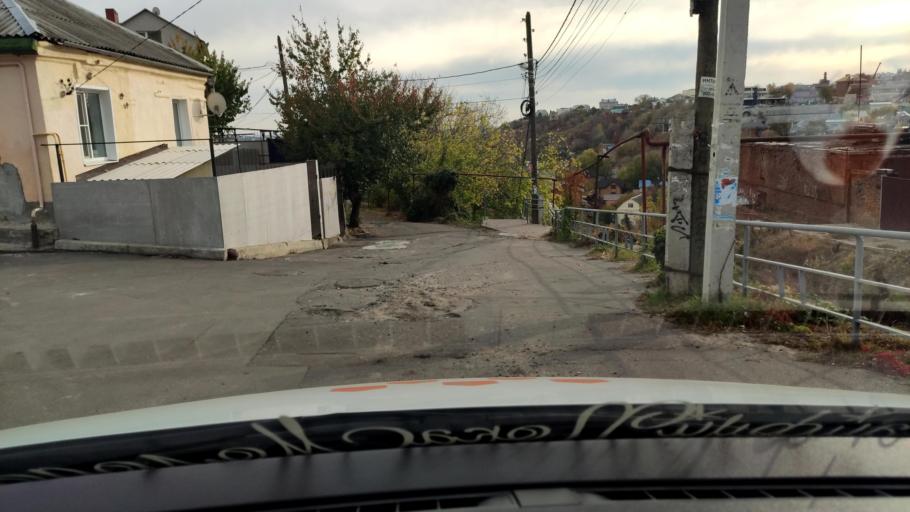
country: RU
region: Voronezj
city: Voronezh
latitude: 51.6539
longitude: 39.2069
